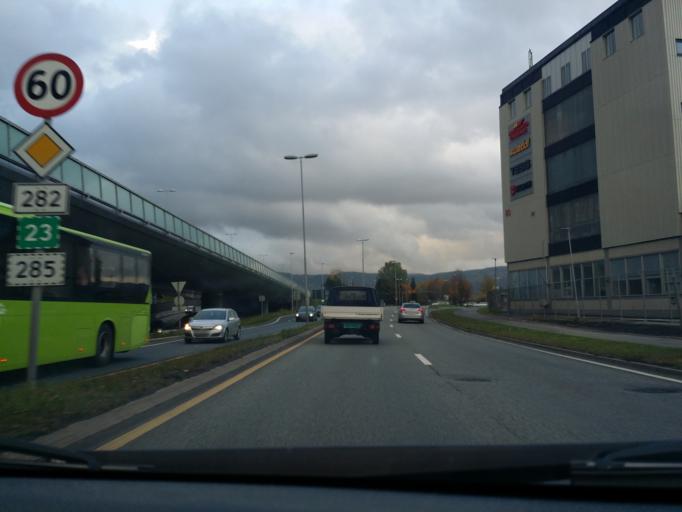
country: NO
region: Buskerud
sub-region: Drammen
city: Drammen
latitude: 59.7431
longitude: 10.2298
